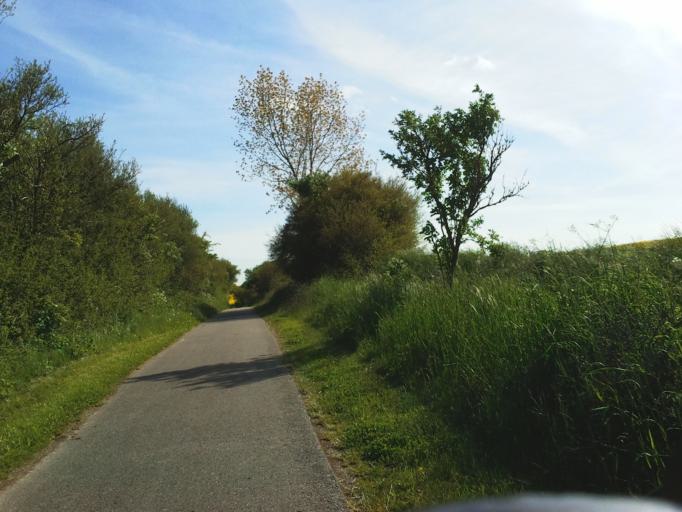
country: DE
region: Mecklenburg-Vorpommern
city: Schwaan
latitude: 53.9668
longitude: 12.1015
